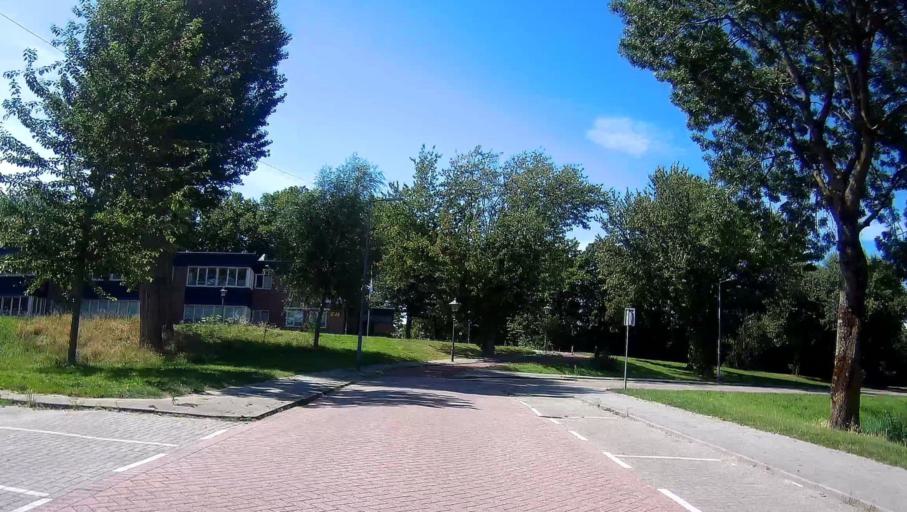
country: NL
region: South Holland
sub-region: Gemeente Capelle aan den IJssel
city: Capelle-West
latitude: 51.8935
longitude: 4.5473
